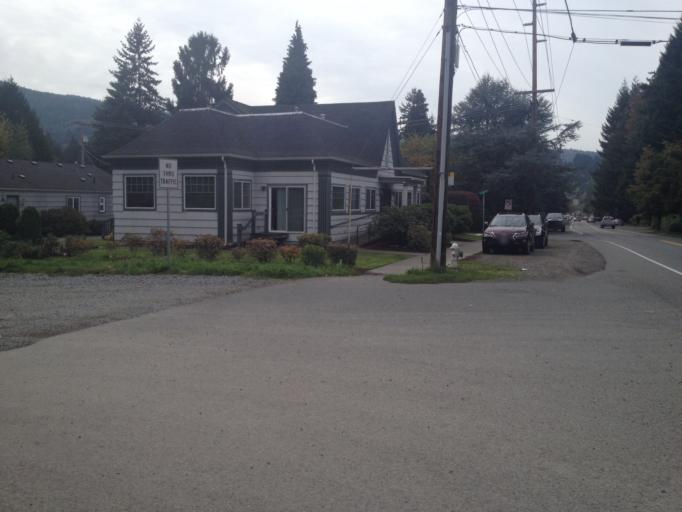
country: US
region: Washington
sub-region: King County
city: Issaquah
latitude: 47.5299
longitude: -122.0256
